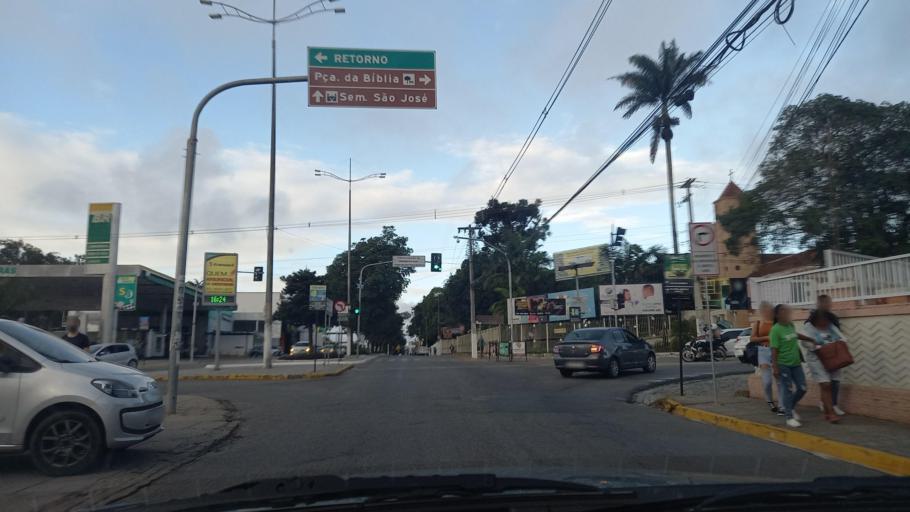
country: BR
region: Pernambuco
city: Garanhuns
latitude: -8.8867
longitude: -36.4865
